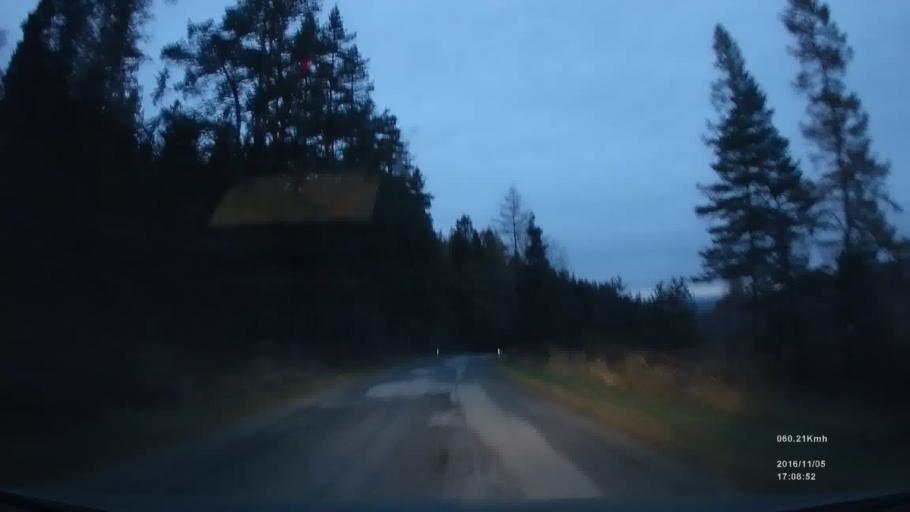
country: SK
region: Presovsky
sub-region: Okres Presov
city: Levoca
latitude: 49.0493
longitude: 20.5185
